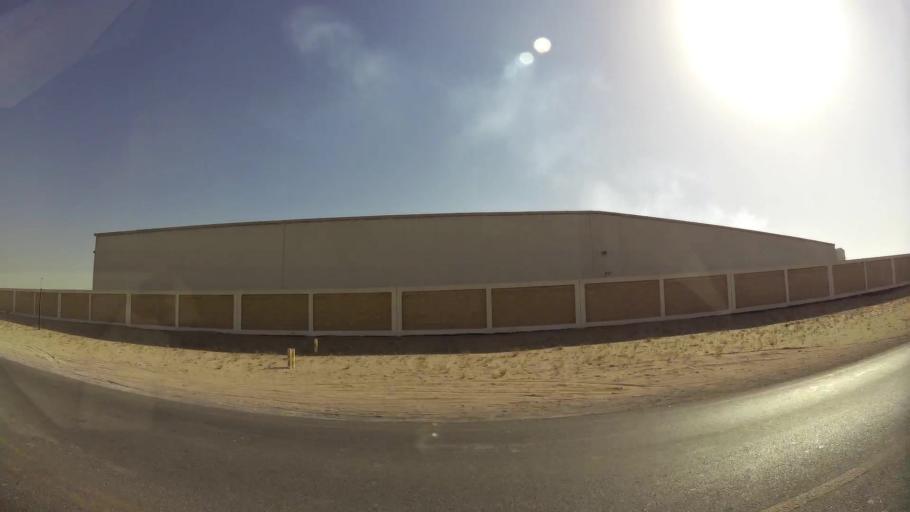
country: AE
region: Dubai
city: Dubai
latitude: 24.9964
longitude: 55.1246
